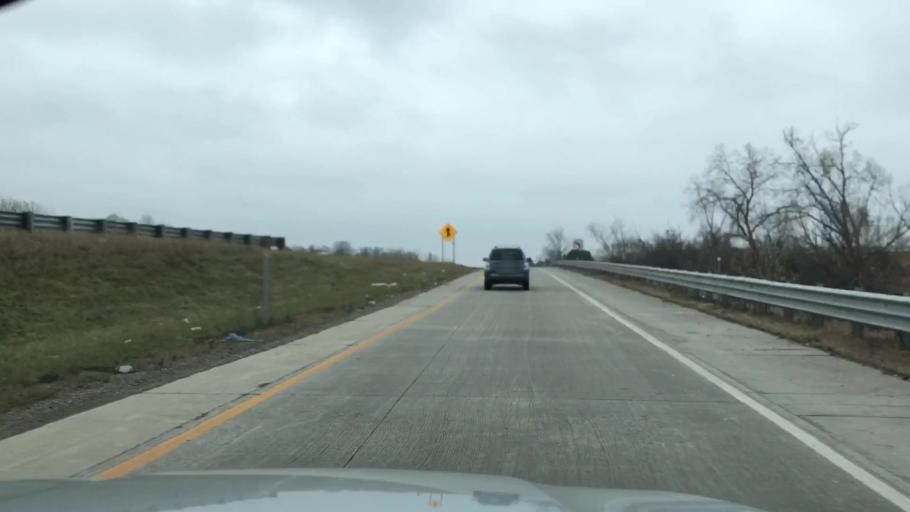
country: US
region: Michigan
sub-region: Wayne County
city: Northville
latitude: 42.4376
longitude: -83.4322
